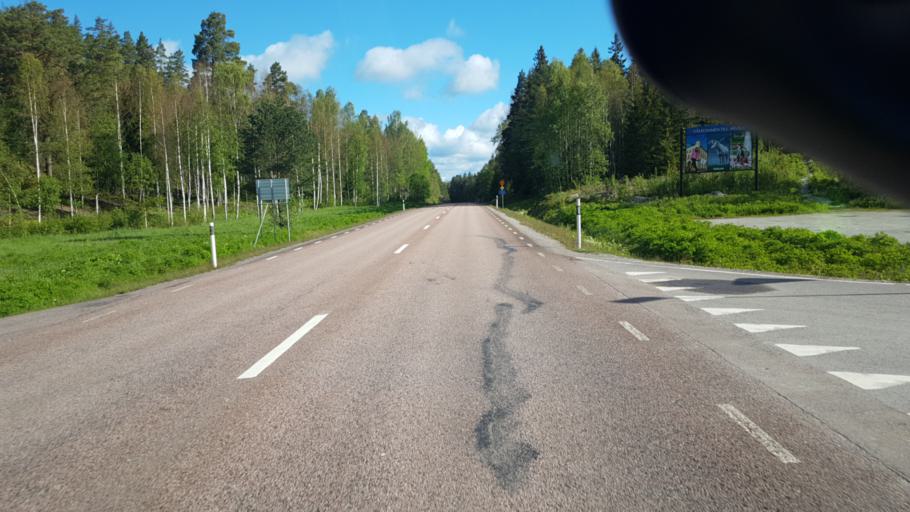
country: SE
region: Vaermland
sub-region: Arvika Kommun
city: Arvika
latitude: 59.6251
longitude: 12.6176
